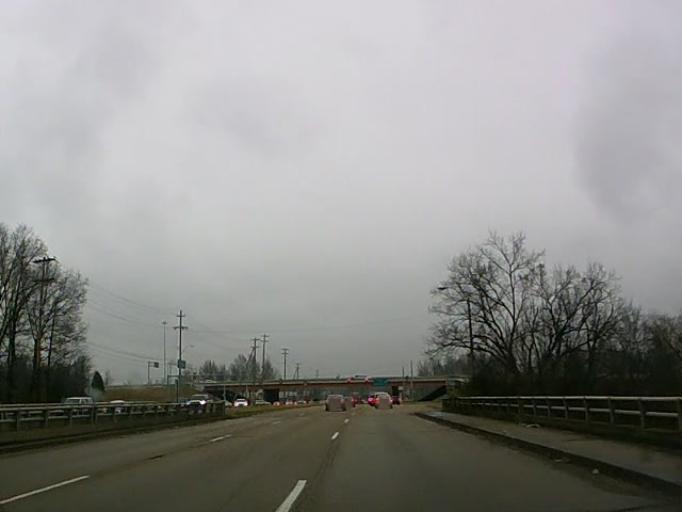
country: US
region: Tennessee
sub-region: Shelby County
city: Germantown
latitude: 35.0736
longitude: -89.8623
